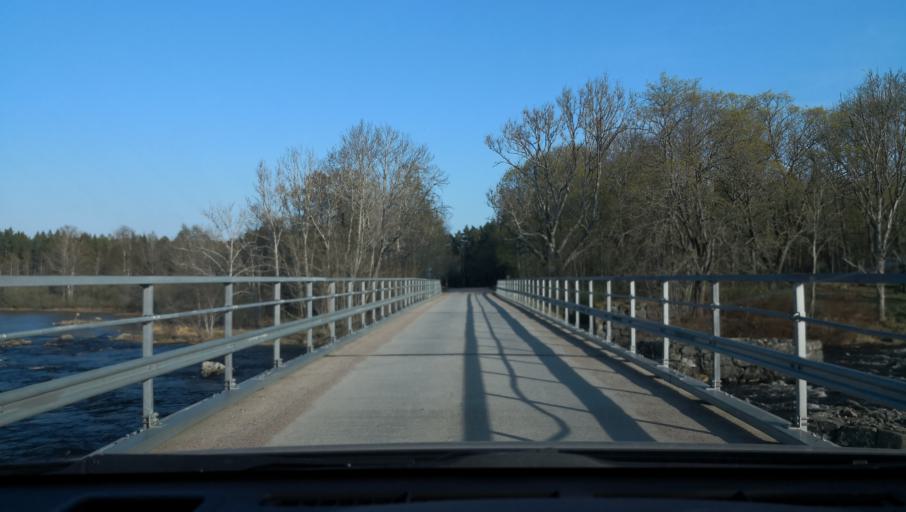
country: SE
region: Uppsala
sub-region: Heby Kommun
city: Tarnsjo
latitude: 60.2676
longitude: 16.9142
